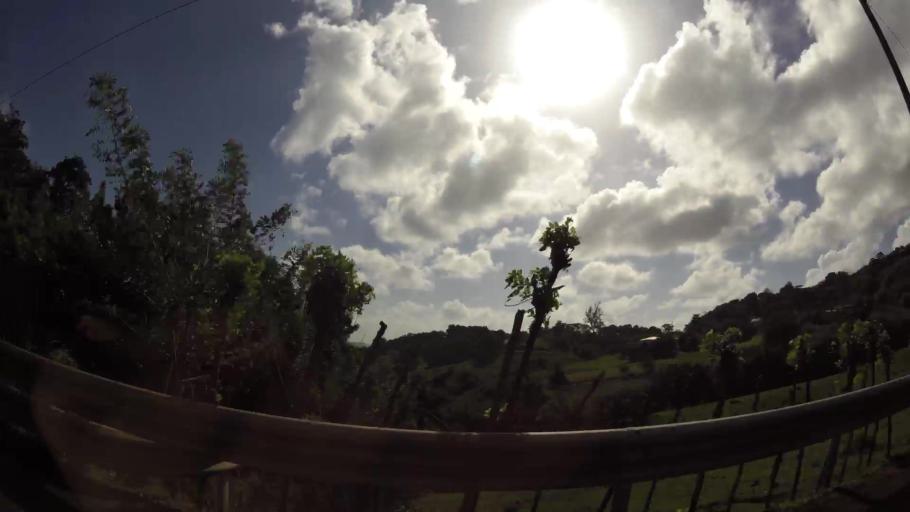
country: MQ
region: Martinique
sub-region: Martinique
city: Sainte-Marie
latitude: 14.7708
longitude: -60.9852
